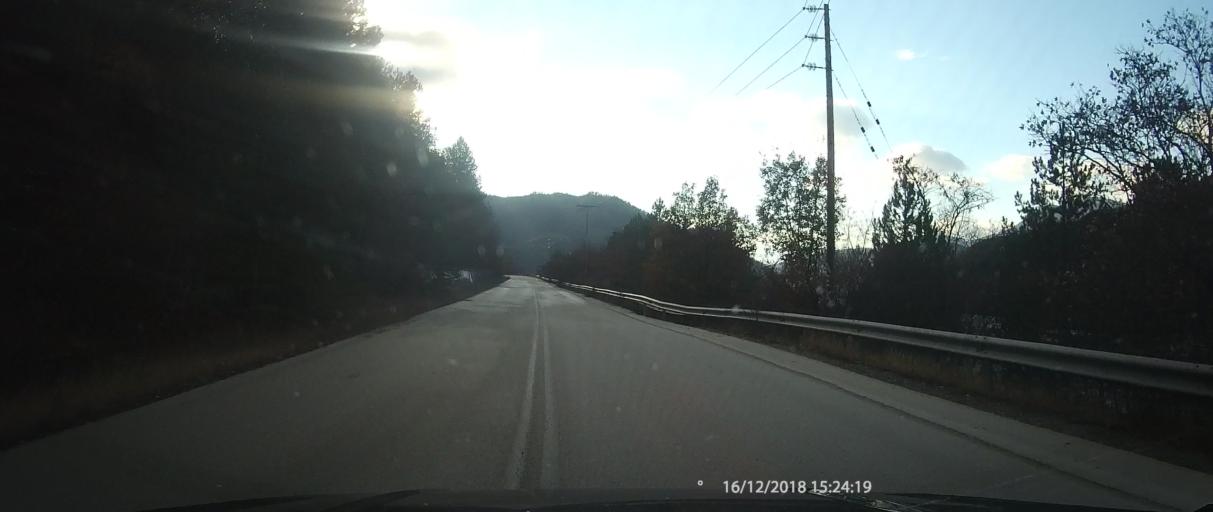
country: GR
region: Epirus
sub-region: Nomos Ioanninon
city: Konitsa
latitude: 40.1394
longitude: 20.7932
